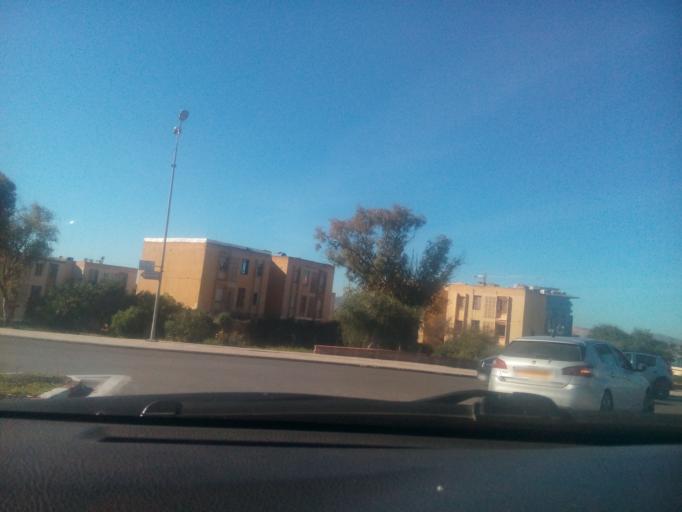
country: DZ
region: Oran
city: Oran
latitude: 35.7163
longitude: -0.6026
